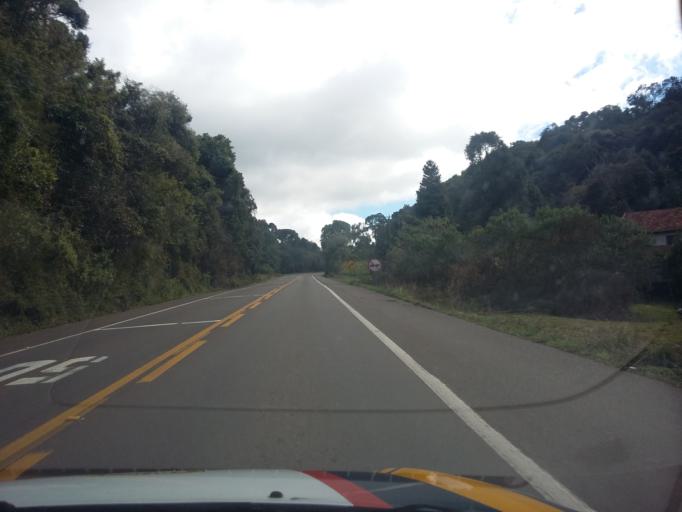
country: BR
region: Rio Grande do Sul
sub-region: Sao Marcos
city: Sao Marcos
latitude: -28.7875
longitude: -51.0963
